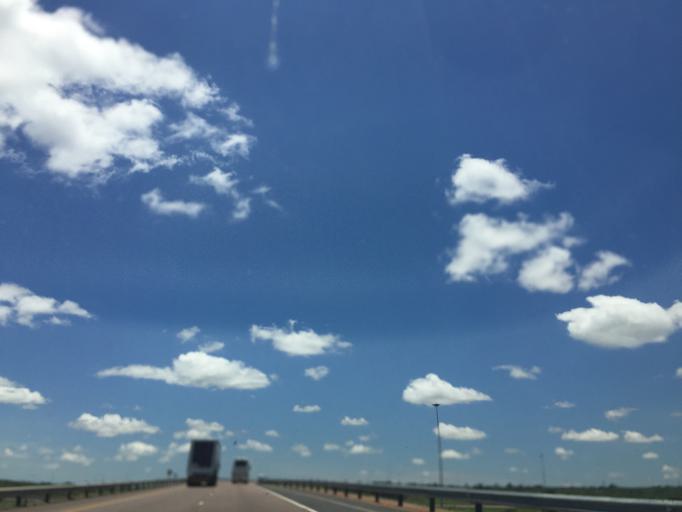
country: ZA
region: Gauteng
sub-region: City of Tshwane Metropolitan Municipality
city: Pretoria
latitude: -25.6435
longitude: 28.2720
